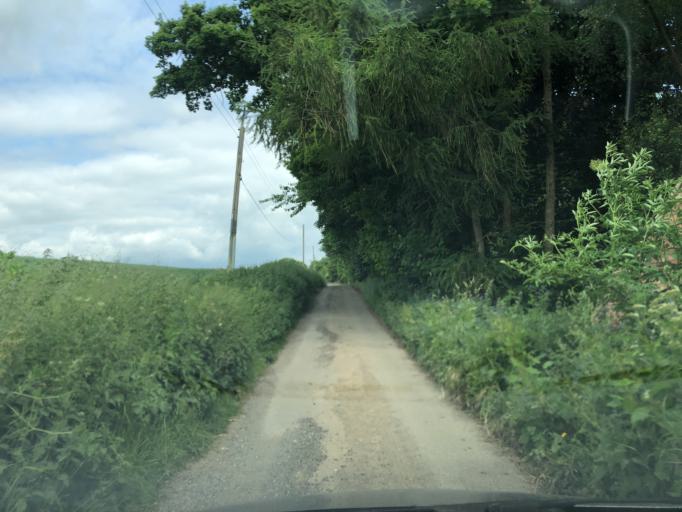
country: GB
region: England
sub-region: North Yorkshire
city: Helmsley
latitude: 54.1578
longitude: -1.0045
